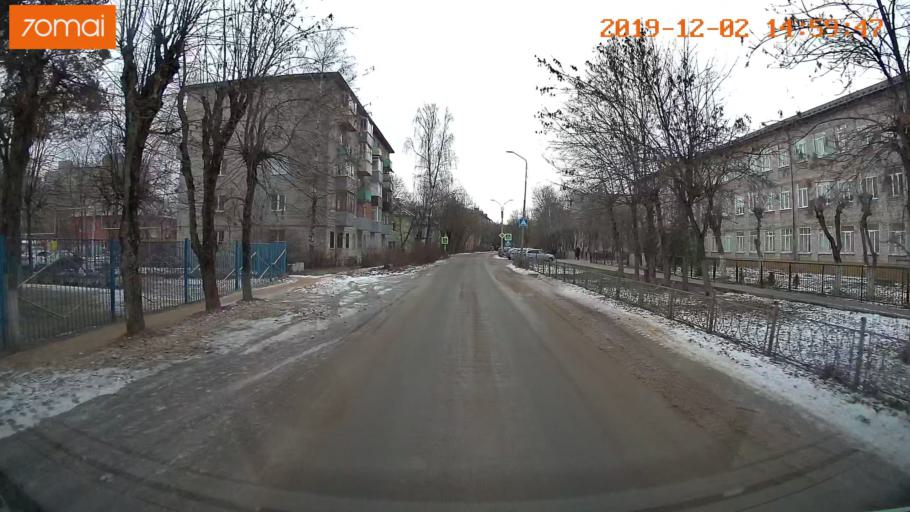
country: RU
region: Ivanovo
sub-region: Gorod Ivanovo
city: Ivanovo
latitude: 56.9712
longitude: 41.0087
